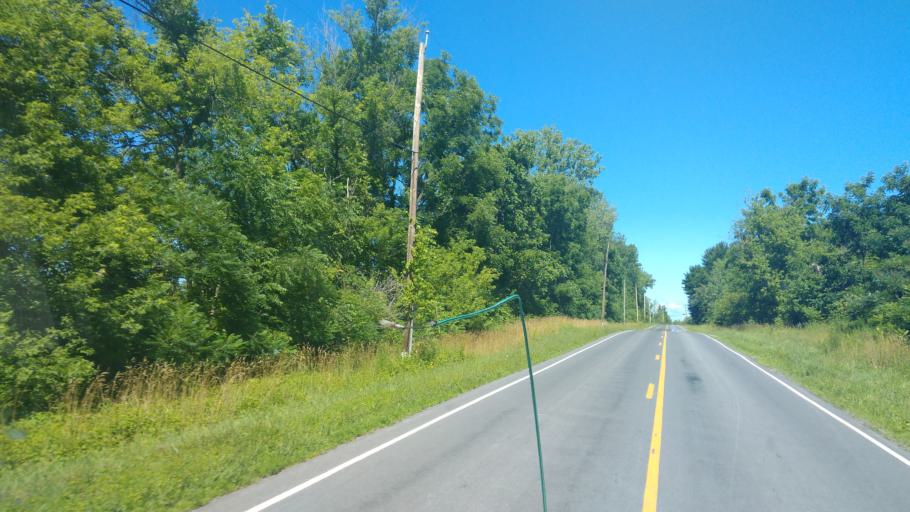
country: US
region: New York
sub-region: Wayne County
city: Sodus
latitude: 43.1829
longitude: -77.0447
